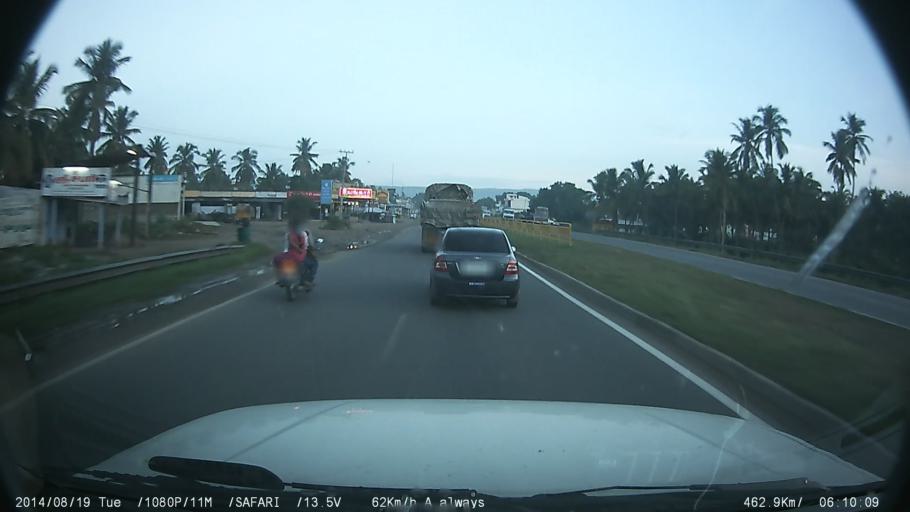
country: IN
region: Tamil Nadu
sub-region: Salem
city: Omalur
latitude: 11.9388
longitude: 78.0521
